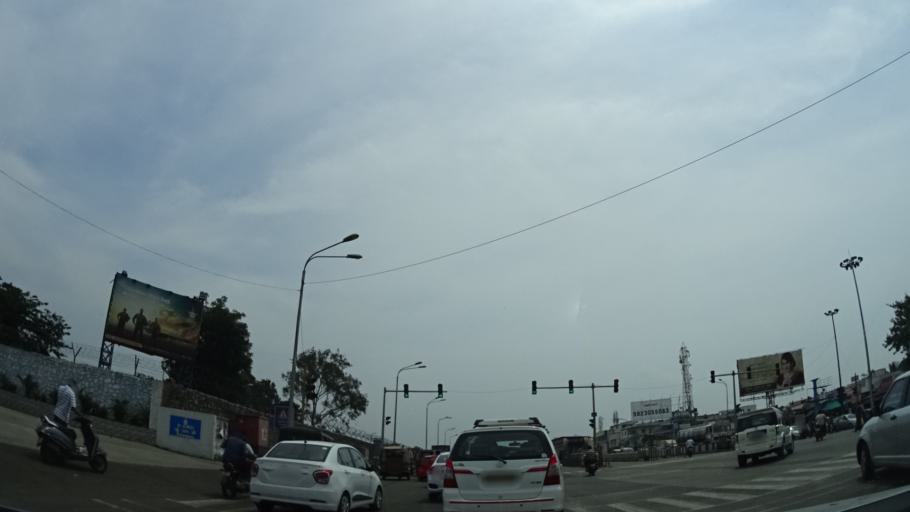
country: IN
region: Maharashtra
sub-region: Pune Division
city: Lohogaon
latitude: 18.5630
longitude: 73.9274
